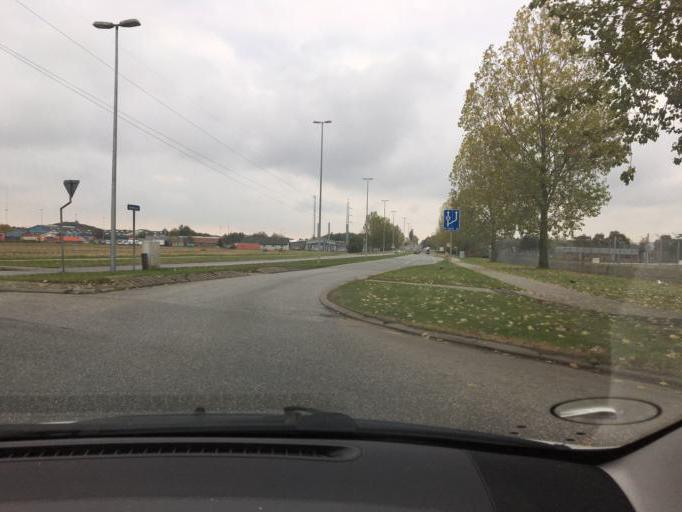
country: DK
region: South Denmark
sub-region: Fredericia Kommune
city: Fredericia
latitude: 55.5930
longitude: 9.7553
